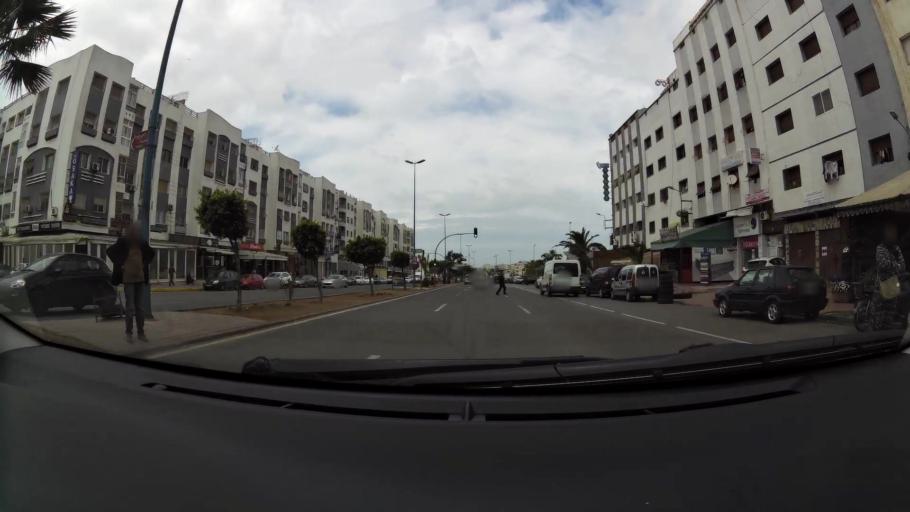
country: MA
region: Grand Casablanca
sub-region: Casablanca
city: Casablanca
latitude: 33.5714
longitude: -7.5617
